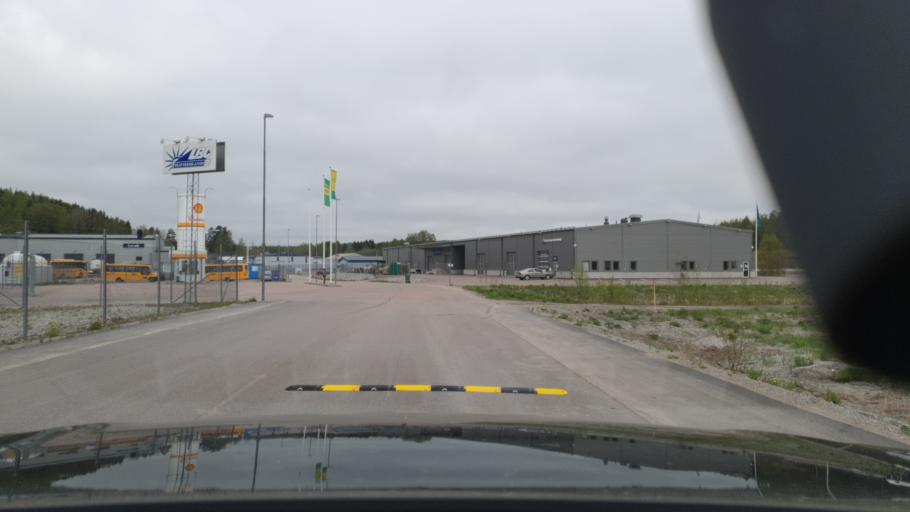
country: SE
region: Vaermland
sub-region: Arvika Kommun
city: Arvika
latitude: 59.6571
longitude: 12.6420
